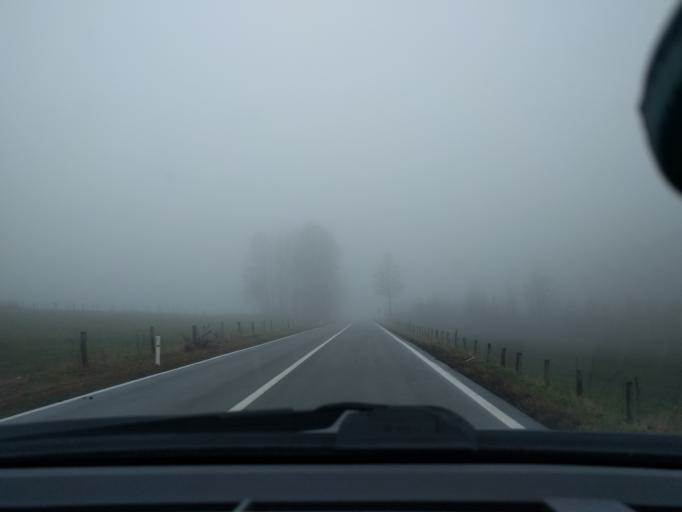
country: BE
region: Wallonia
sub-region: Province du Luxembourg
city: Gouvy
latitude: 50.2087
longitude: 5.9853
